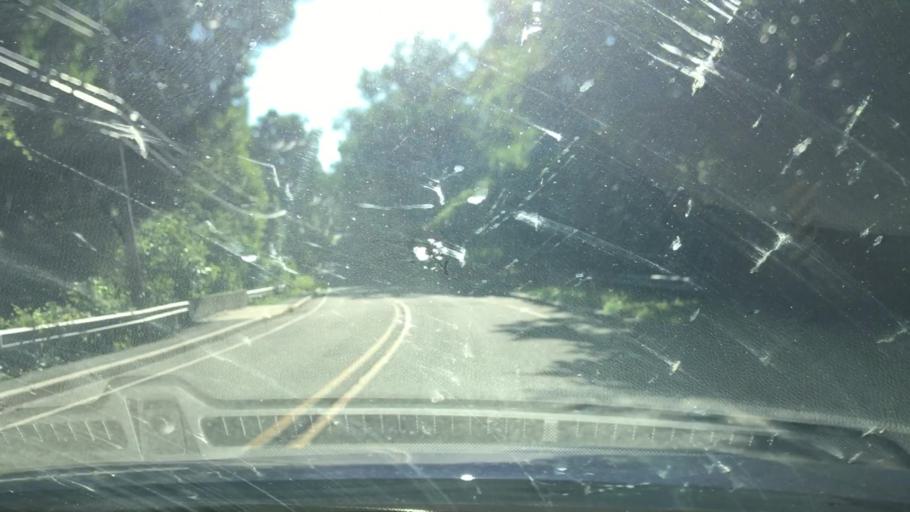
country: US
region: New Jersey
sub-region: Bergen County
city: Alpine
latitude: 40.9429
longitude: -73.9377
